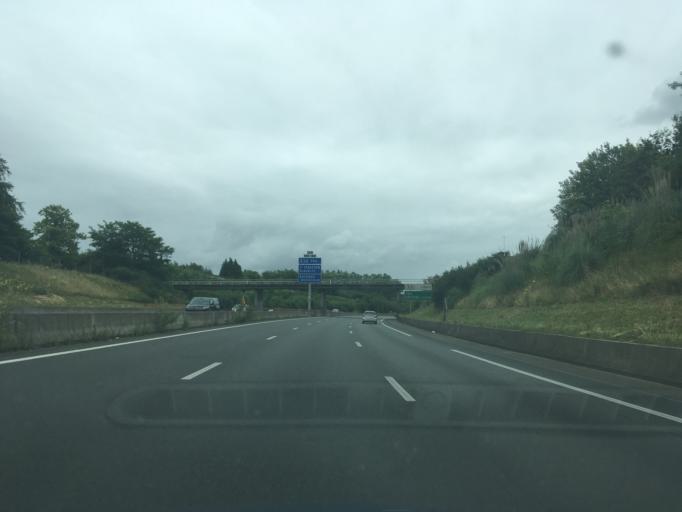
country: FR
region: Aquitaine
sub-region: Departement des Pyrenees-Atlantiques
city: Boucau
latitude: 43.5038
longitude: -1.4401
